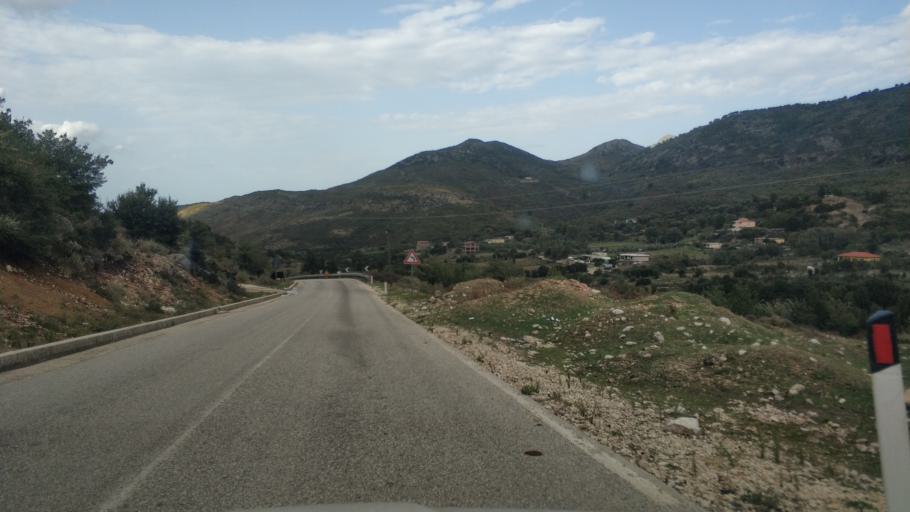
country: AL
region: Vlore
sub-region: Rrethi i Vlores
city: Orikum
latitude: 40.2672
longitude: 19.5158
